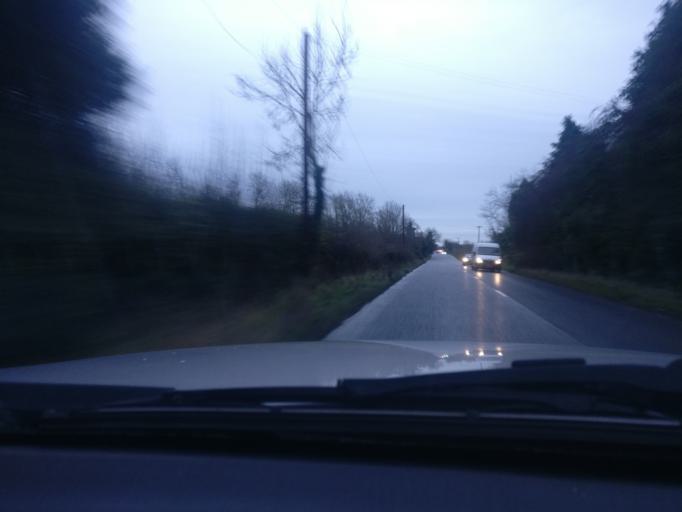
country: IE
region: Leinster
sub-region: An Mhi
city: Navan
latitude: 53.6777
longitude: -6.7505
